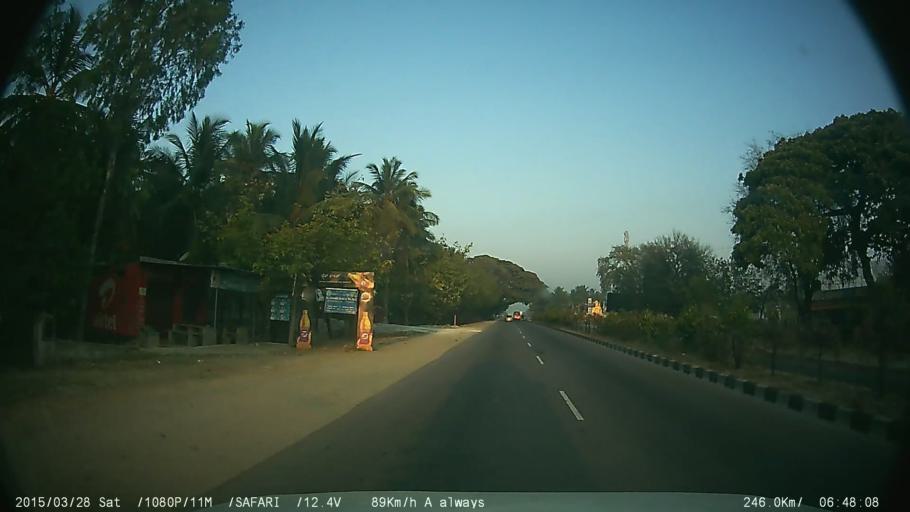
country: IN
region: Karnataka
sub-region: Mandya
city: Maddur
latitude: 12.6132
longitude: 77.0697
